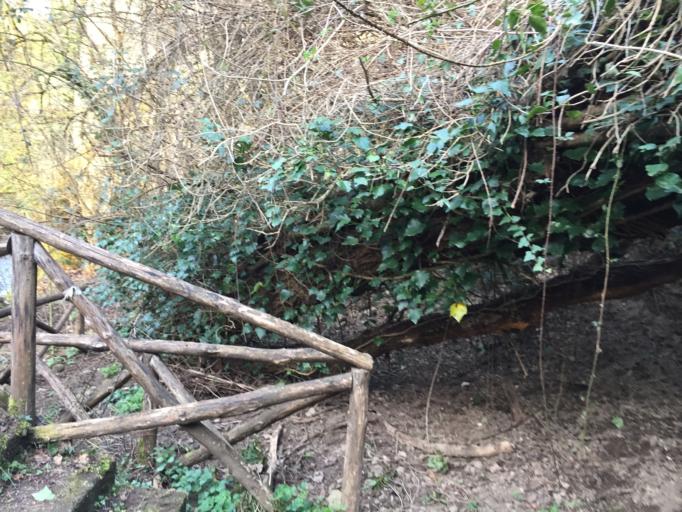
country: IT
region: Latium
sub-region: Provincia di Viterbo
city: Calcata Nuova
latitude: 42.2173
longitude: 12.4190
